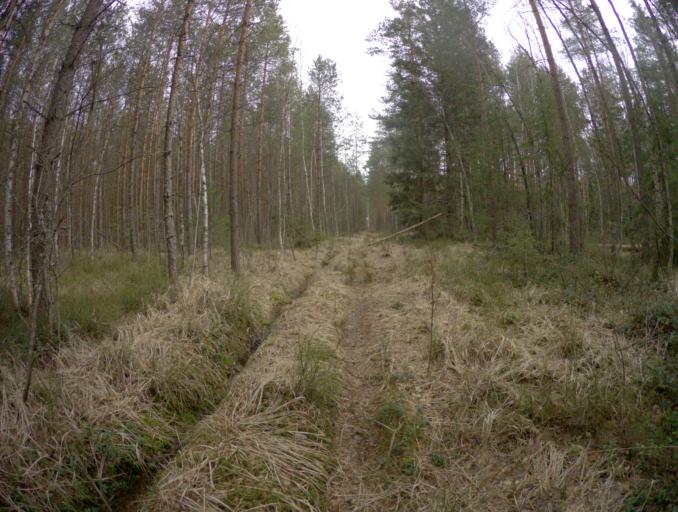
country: RU
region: Vladimir
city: Raduzhnyy
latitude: 55.9528
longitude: 40.2861
